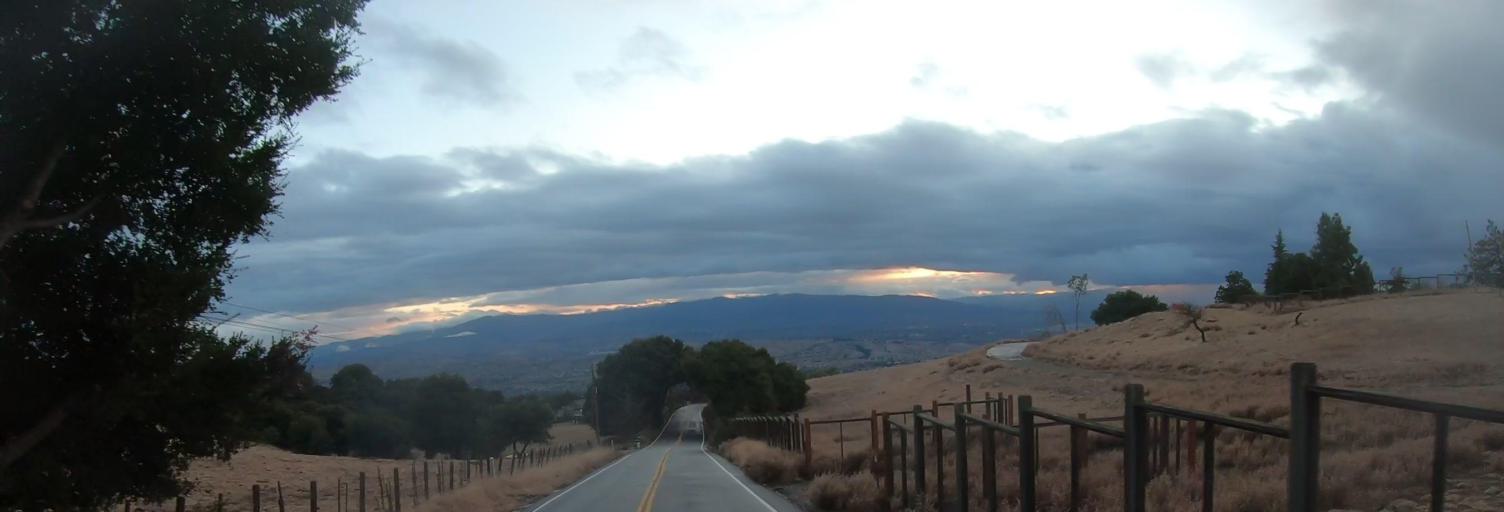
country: US
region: California
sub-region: Santa Clara County
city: East Foothills
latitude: 37.3299
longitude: -121.7451
